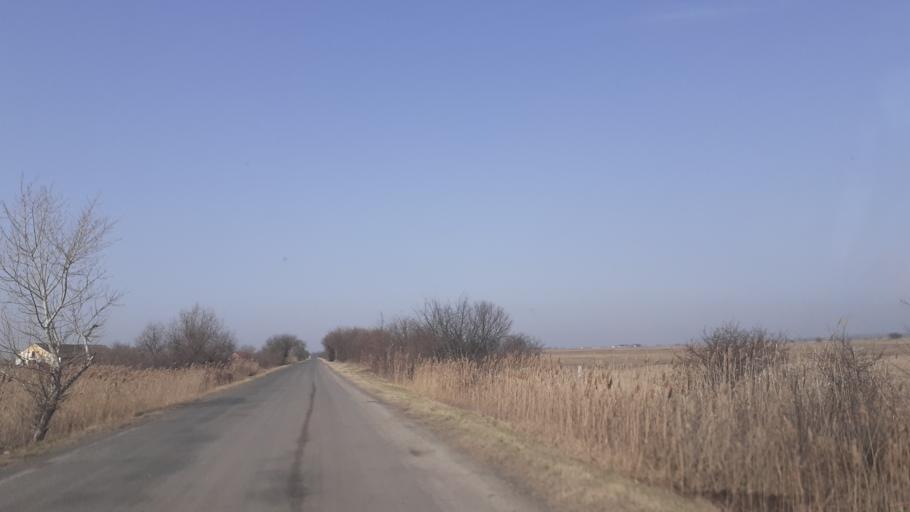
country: HU
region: Pest
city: Bugyi
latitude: 47.1277
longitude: 19.2077
